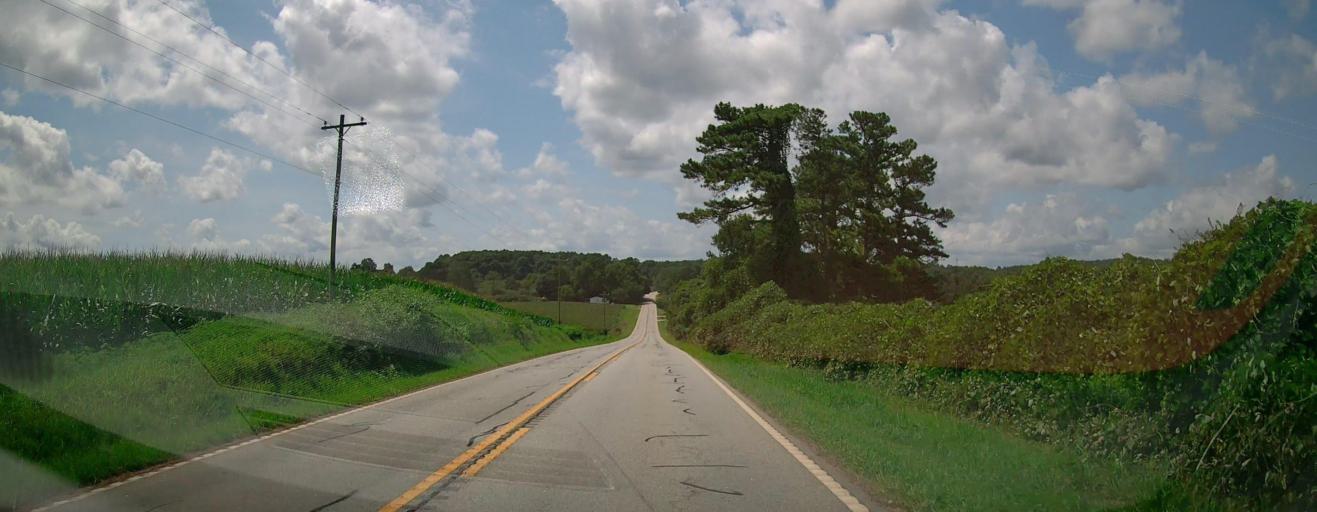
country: US
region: Georgia
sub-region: Carroll County
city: Bowdon
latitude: 33.4153
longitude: -85.2601
